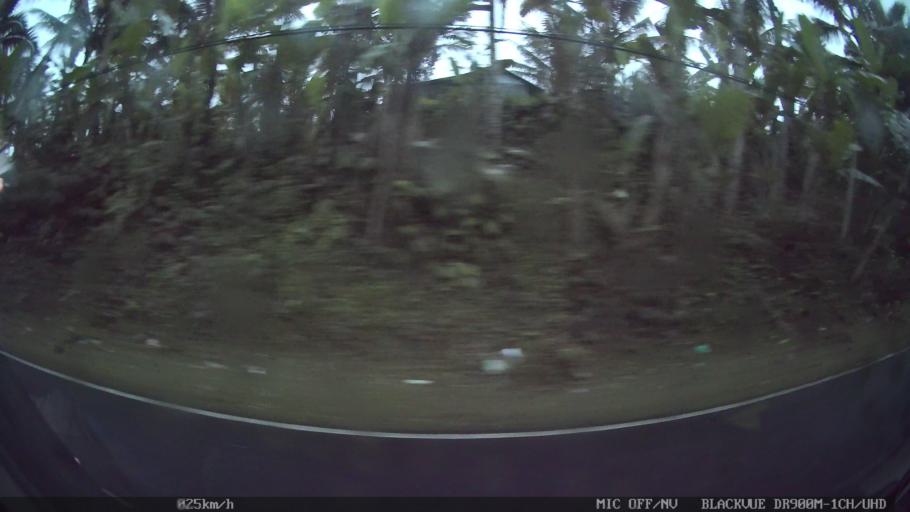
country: ID
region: Bali
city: Banjar Taro Kelod
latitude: -8.3663
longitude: 115.2705
